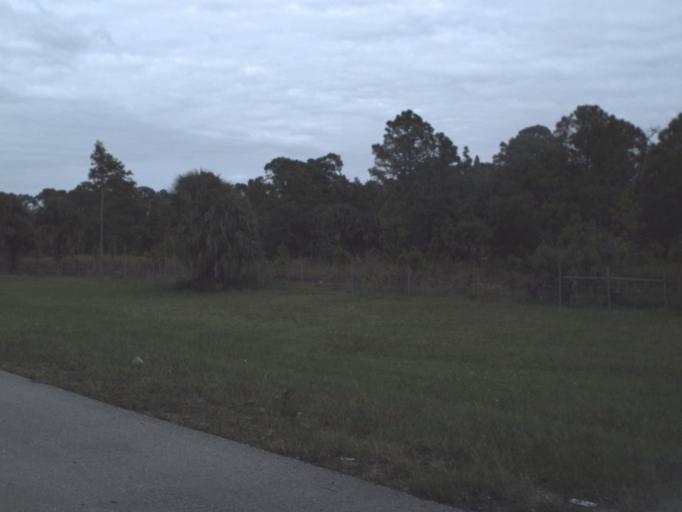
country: US
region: Florida
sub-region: Collier County
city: Vineyards
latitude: 26.2010
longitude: -81.7357
